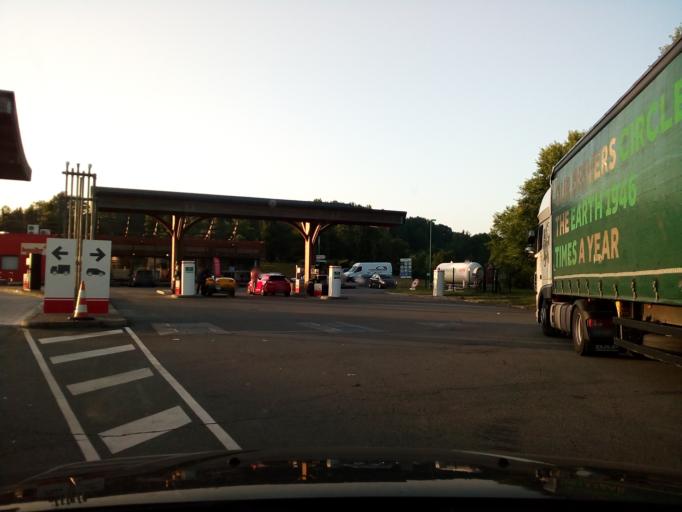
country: FR
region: Limousin
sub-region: Departement de la Creuse
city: Saint-Sulpice-le-Gueretois
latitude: 46.1832
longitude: 1.8454
